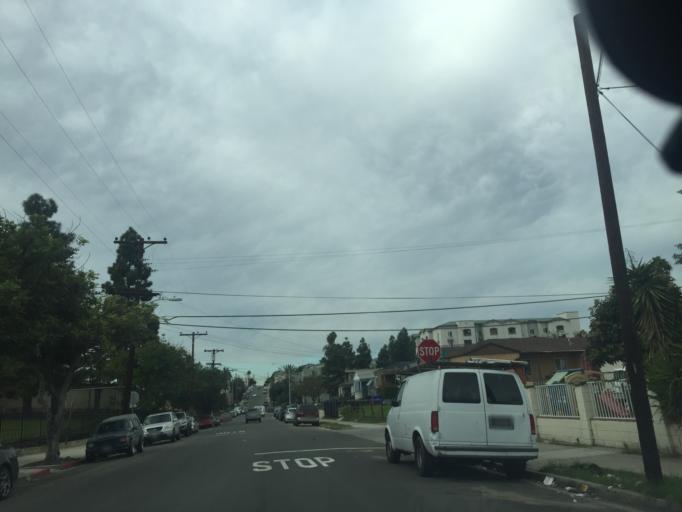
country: US
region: California
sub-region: San Diego County
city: Lemon Grove
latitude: 32.7549
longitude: -117.0811
